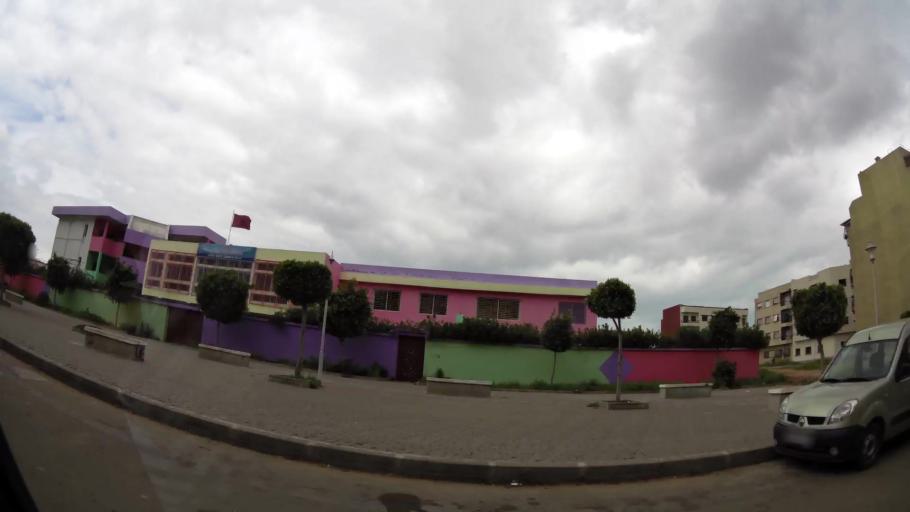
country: MA
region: Grand Casablanca
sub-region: Mediouna
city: Tit Mellil
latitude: 33.5681
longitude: -7.5488
